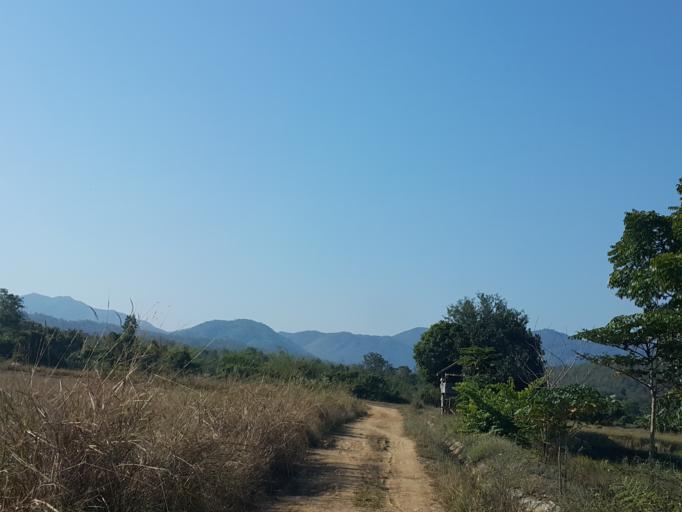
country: TH
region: Sukhothai
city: Thung Saliam
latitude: 17.3131
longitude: 99.4348
